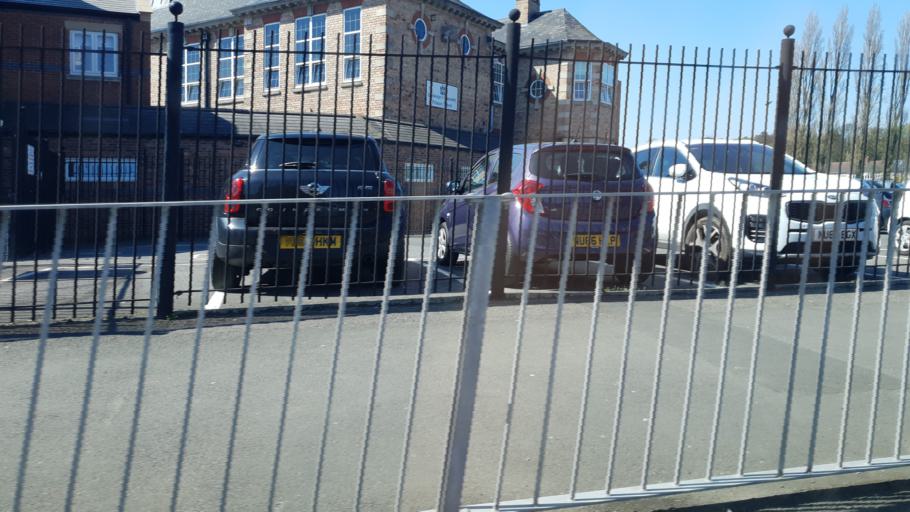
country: GB
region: England
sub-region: Middlesbrough
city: Middlesbrough
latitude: 54.5588
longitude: -1.2483
